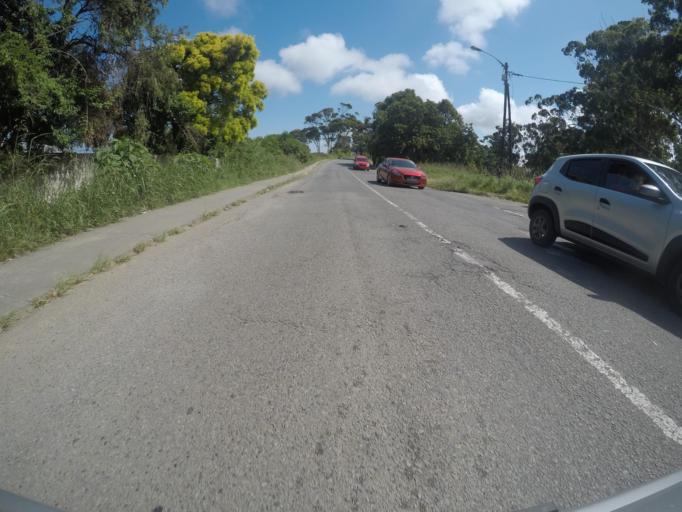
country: ZA
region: Eastern Cape
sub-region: Buffalo City Metropolitan Municipality
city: East London
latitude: -32.9988
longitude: 27.8920
